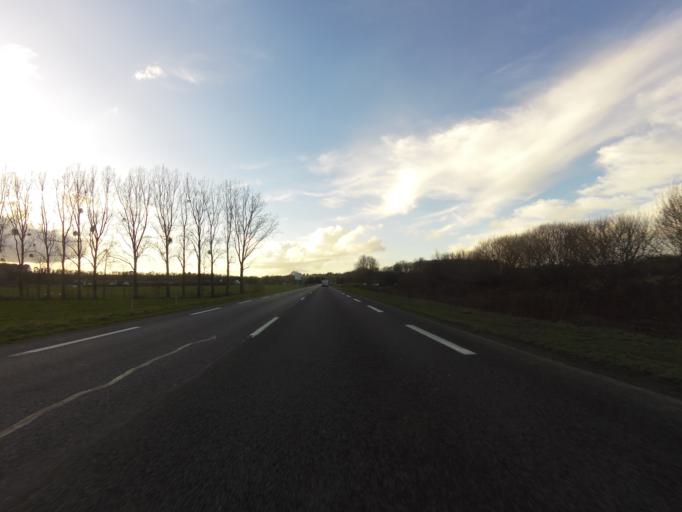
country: FR
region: Brittany
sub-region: Departement du Morbihan
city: Lanouee
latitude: 47.9639
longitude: -2.6114
